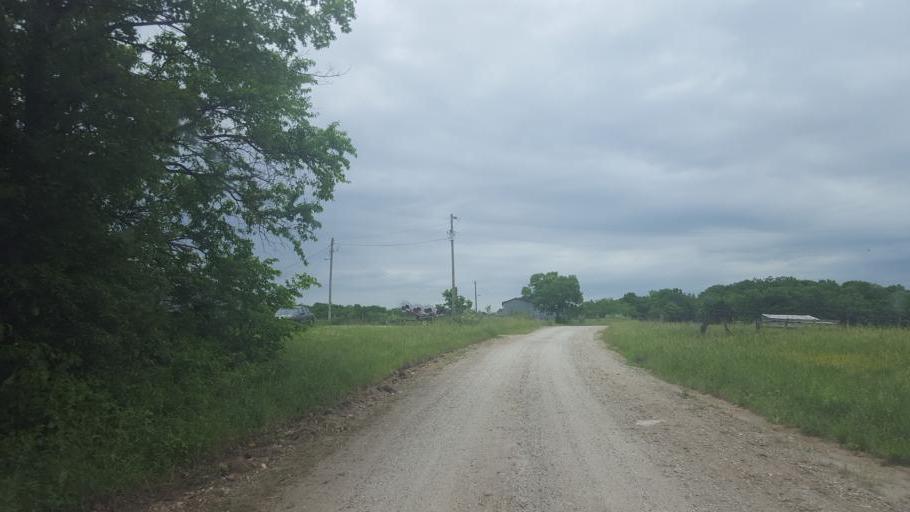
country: US
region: Missouri
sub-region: Moniteau County
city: California
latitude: 38.7381
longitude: -92.6087
